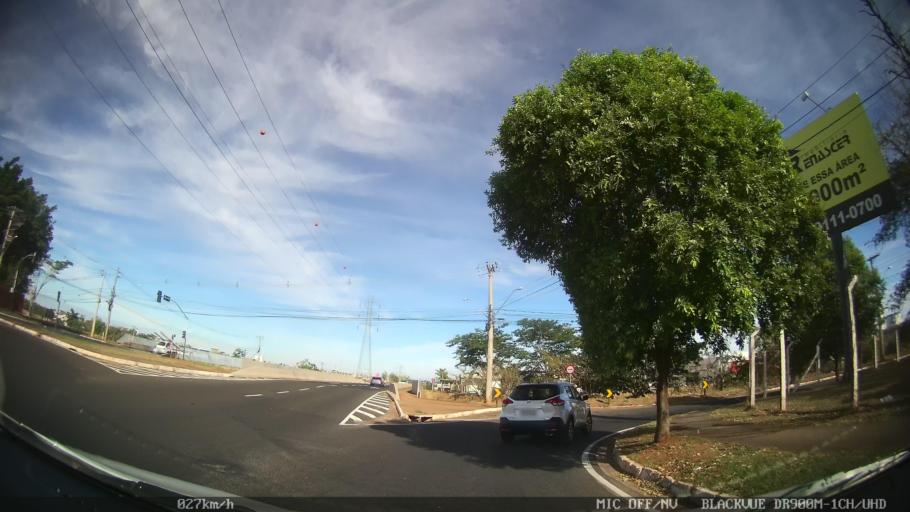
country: BR
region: Sao Paulo
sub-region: Sao Jose Do Rio Preto
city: Sao Jose do Rio Preto
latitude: -20.8010
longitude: -49.3461
